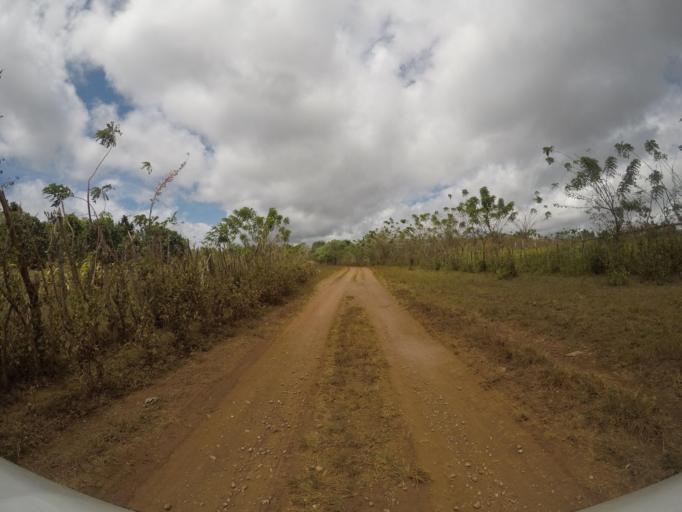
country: TL
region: Lautem
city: Lospalos
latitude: -8.4737
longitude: 126.9898
